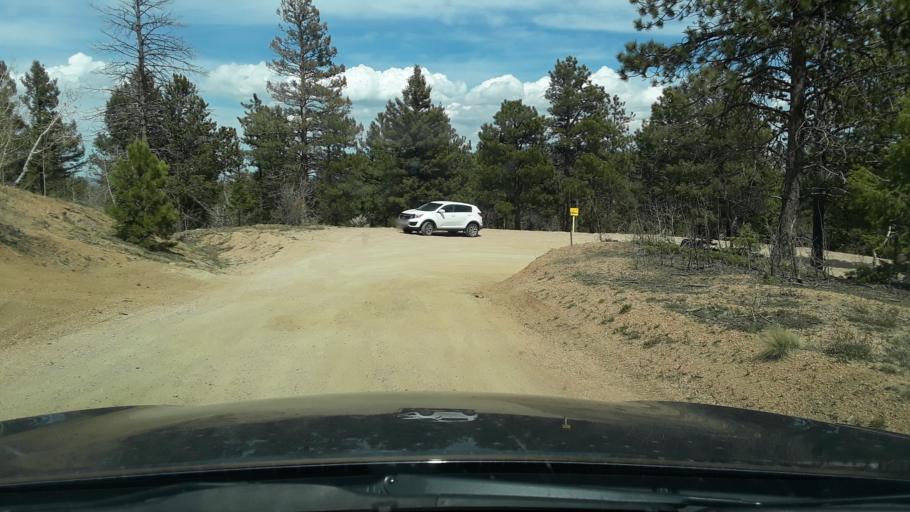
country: US
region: Colorado
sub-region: El Paso County
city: Palmer Lake
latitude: 39.0709
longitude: -104.9503
